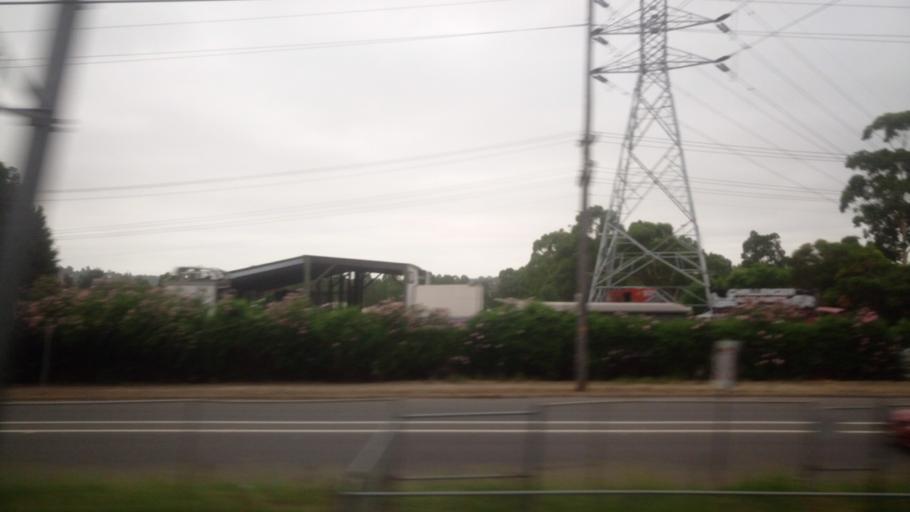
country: AU
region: New South Wales
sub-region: Holroyd
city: Girraween
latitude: -33.7801
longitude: 150.9474
